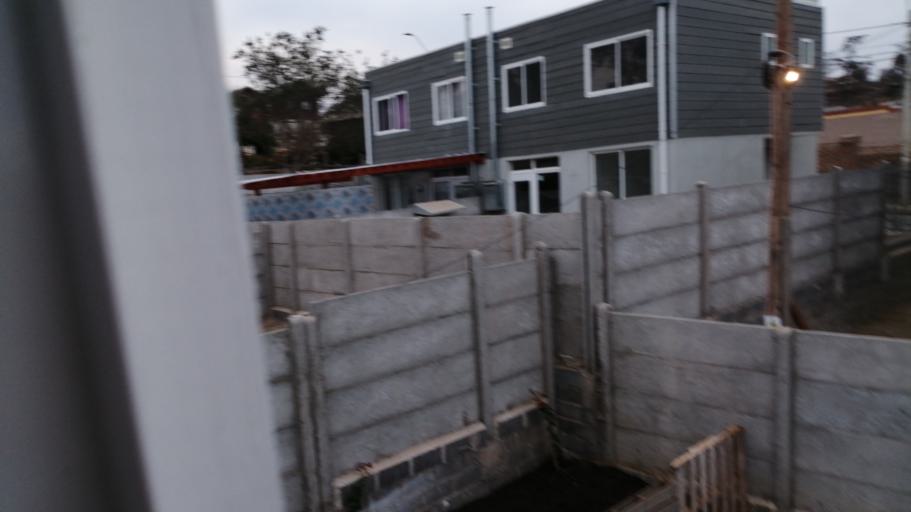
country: CL
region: Valparaiso
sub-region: Provincia de Marga Marga
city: Villa Alemana
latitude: -33.0377
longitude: -71.3600
